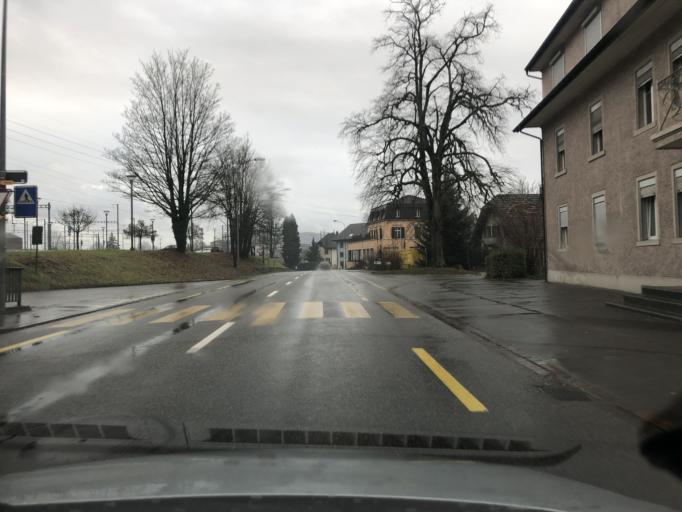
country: CH
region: Aargau
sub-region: Bezirk Zurzach
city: Koblenz
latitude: 47.6000
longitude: 8.2263
